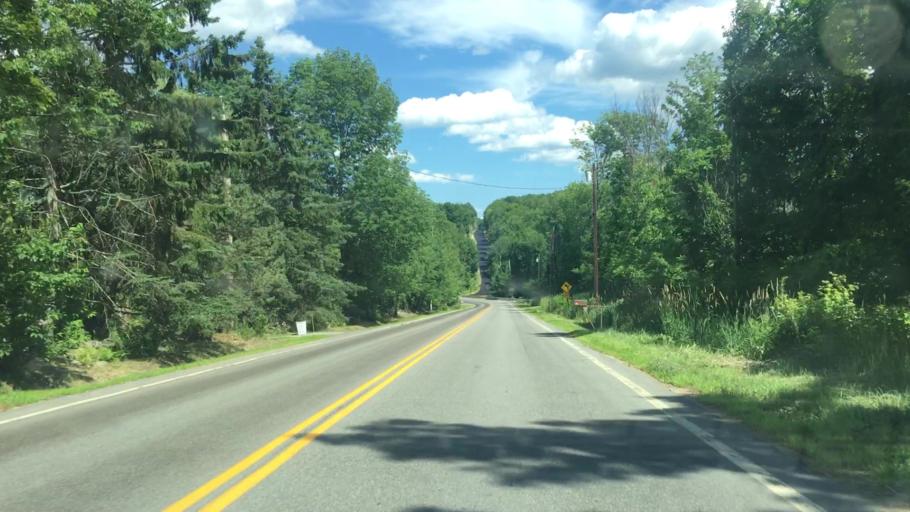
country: US
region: Maine
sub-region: Franklin County
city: Wilton
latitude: 44.5760
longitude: -70.1679
